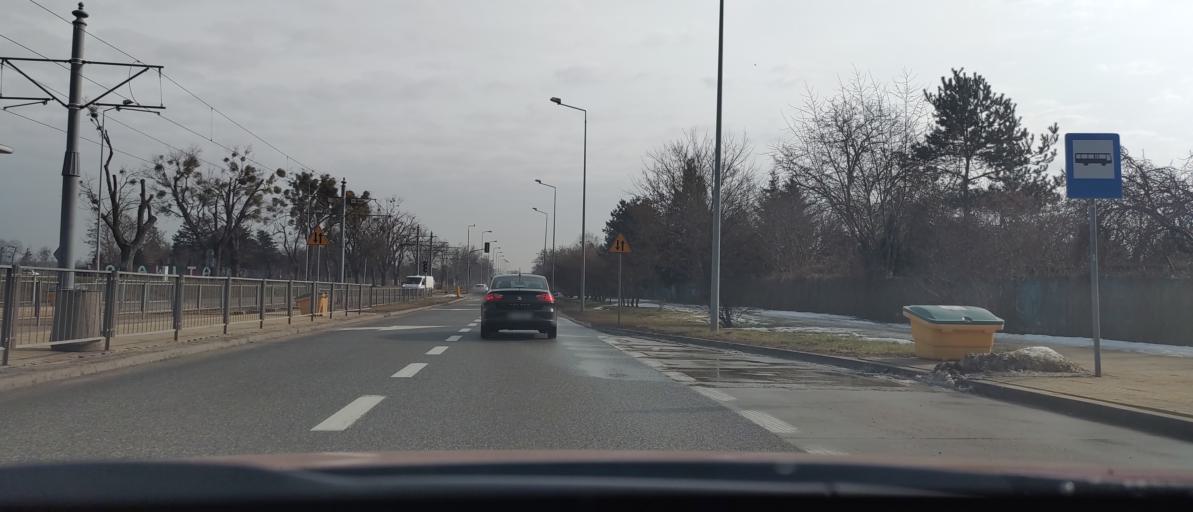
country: PL
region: Masovian Voivodeship
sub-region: Warszawa
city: Bemowo
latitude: 52.2472
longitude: 20.9250
